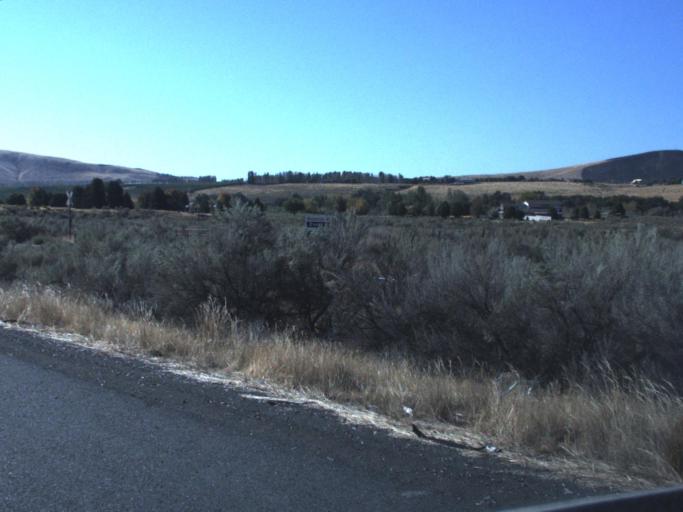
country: US
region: Washington
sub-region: Benton County
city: Richland
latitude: 46.2861
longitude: -119.3067
